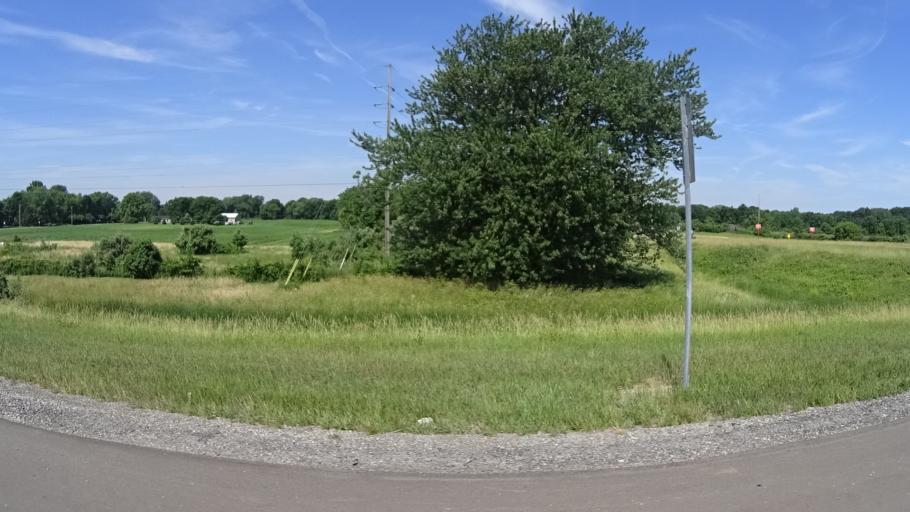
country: US
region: Ohio
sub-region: Erie County
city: Huron
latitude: 41.3667
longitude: -82.4945
